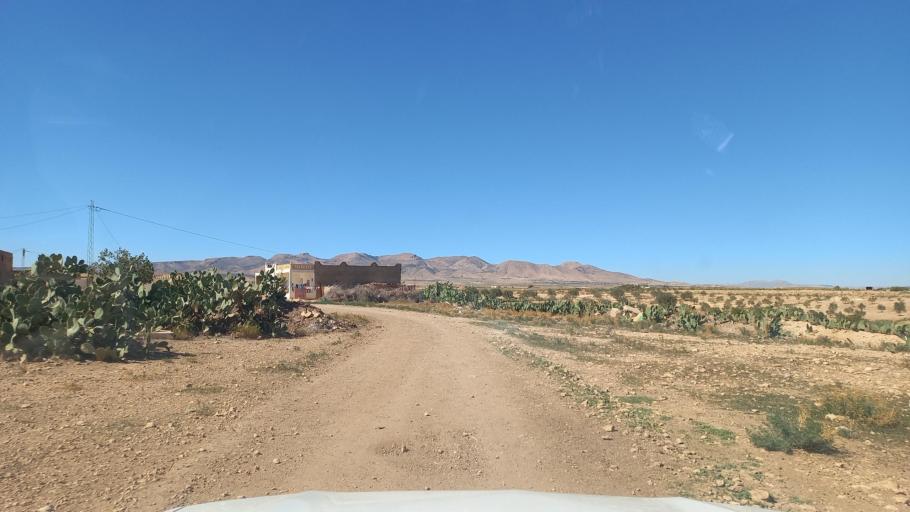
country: TN
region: Al Qasrayn
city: Sbiba
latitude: 35.3810
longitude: 9.0888
